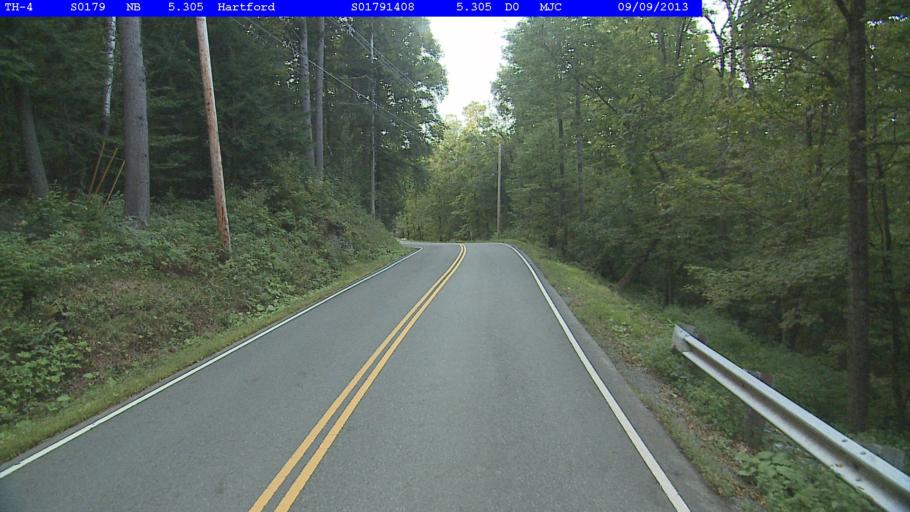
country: US
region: Vermont
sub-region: Windsor County
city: White River Junction
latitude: 43.7048
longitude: -72.4202
